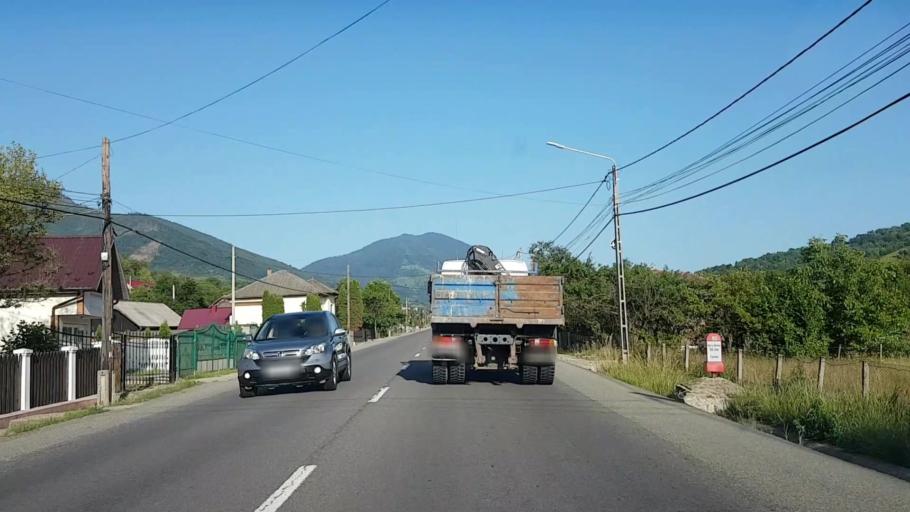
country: RO
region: Bistrita-Nasaud
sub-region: Comuna Tiha Bargaului
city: Tureac
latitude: 47.2264
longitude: 24.8109
